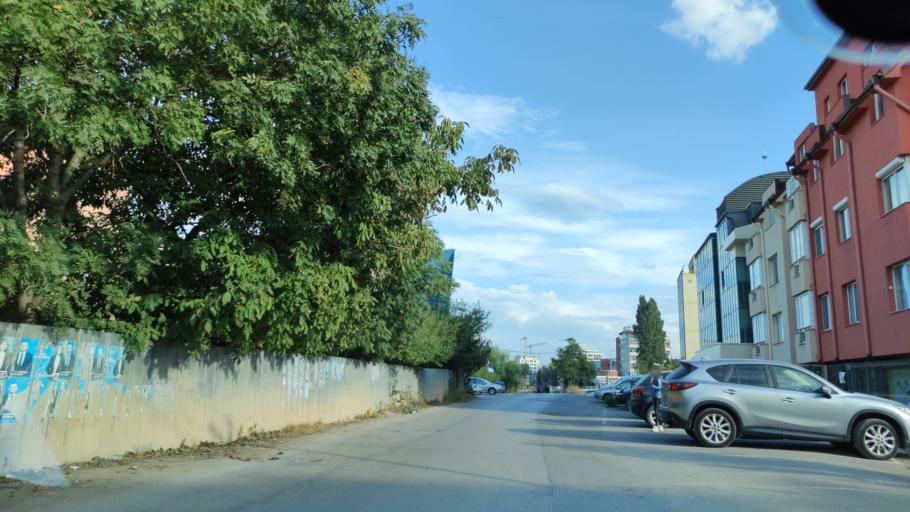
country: BG
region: Sofia-Capital
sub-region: Stolichna Obshtina
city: Sofia
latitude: 42.6582
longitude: 23.2823
